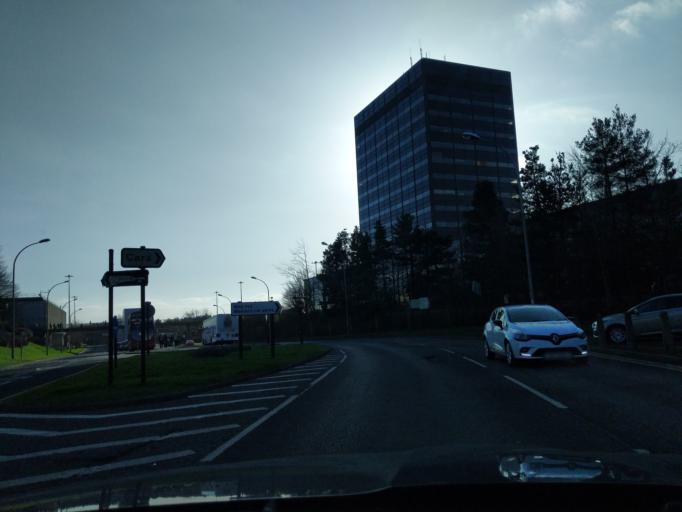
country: GB
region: England
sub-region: Sunderland
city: Washington
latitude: 54.9012
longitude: -1.5347
